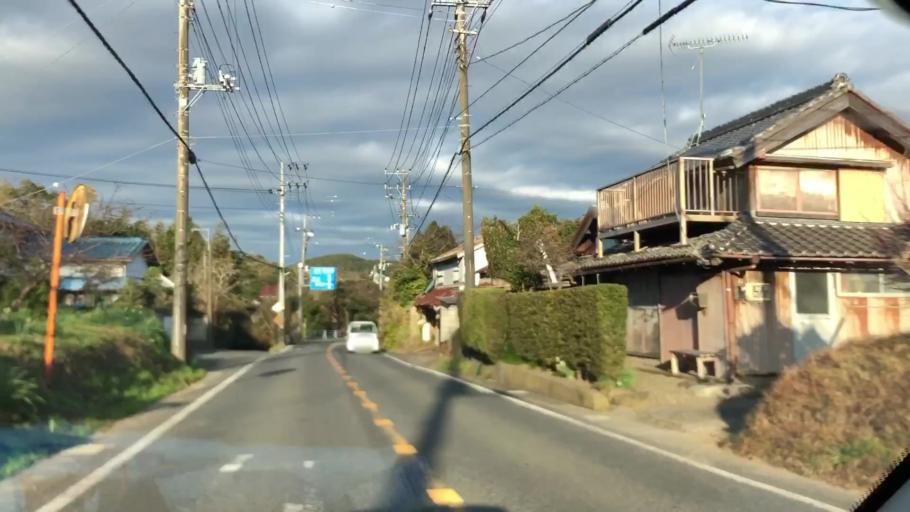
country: JP
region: Chiba
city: Tateyama
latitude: 34.9822
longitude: 139.9463
